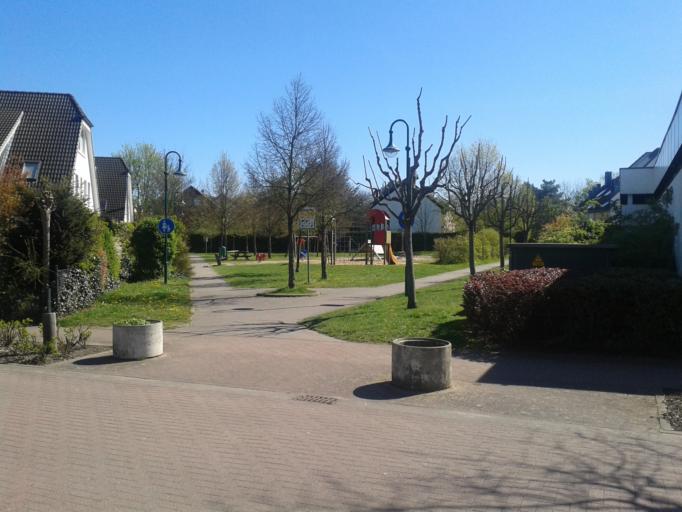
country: DE
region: Schleswig-Holstein
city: Halstenbek
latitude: 53.6018
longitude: 9.8135
